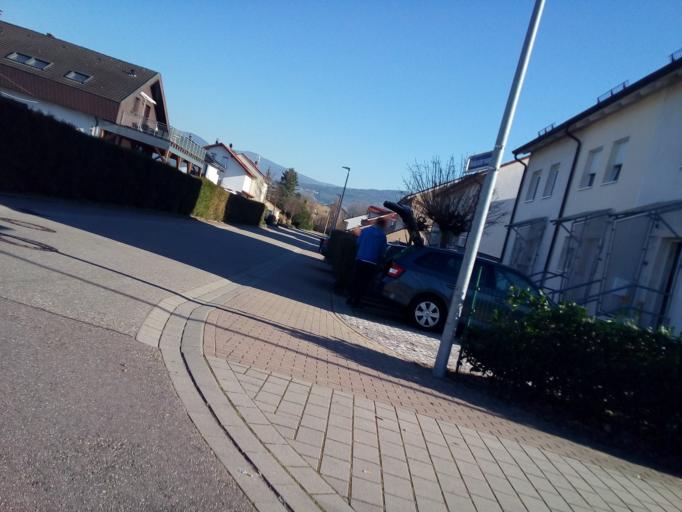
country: DE
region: Baden-Wuerttemberg
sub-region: Karlsruhe Region
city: Buhl
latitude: 48.7034
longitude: 8.1301
